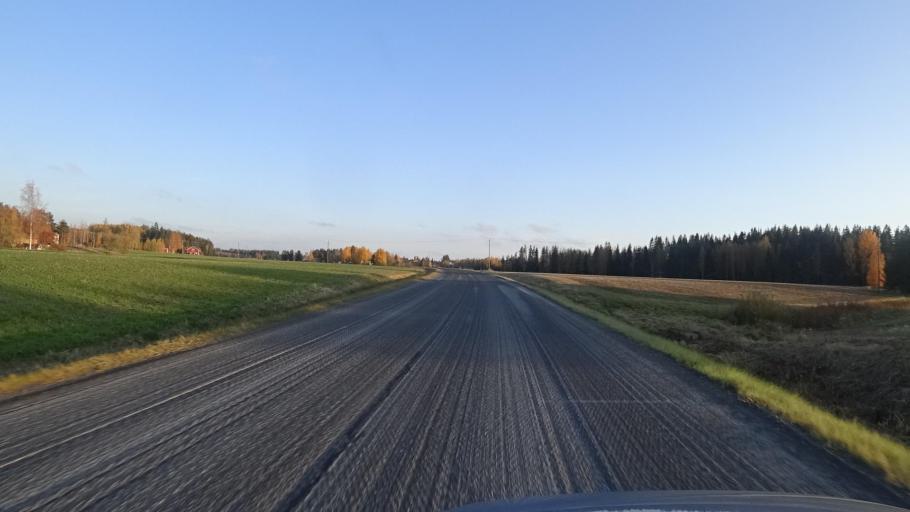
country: FI
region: Haeme
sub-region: Forssa
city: Ypaejae
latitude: 60.7810
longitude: 23.3081
